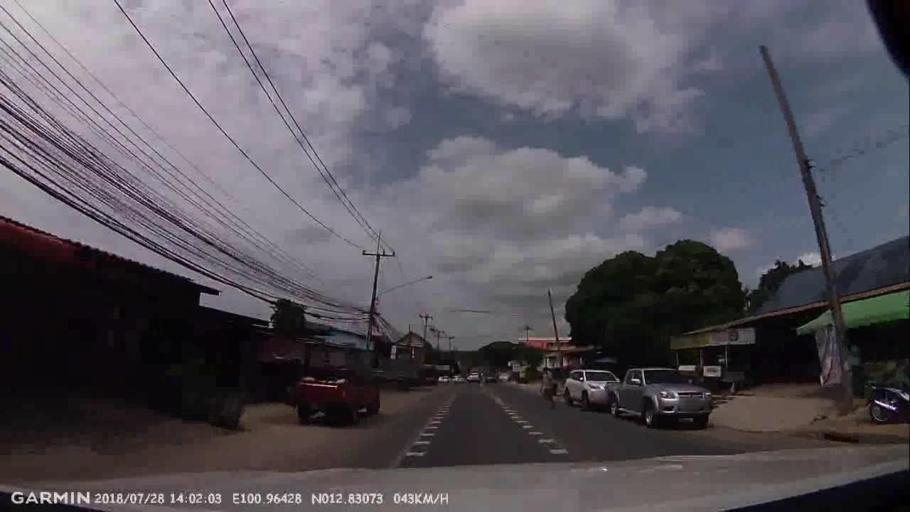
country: TH
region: Chon Buri
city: Phatthaya
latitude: 12.8308
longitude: 100.9644
